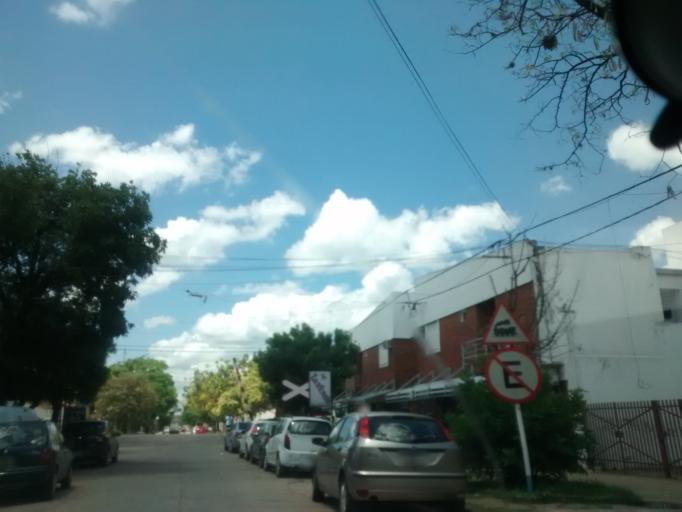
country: AR
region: Chaco
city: Resistencia
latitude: -27.4561
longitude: -58.9903
